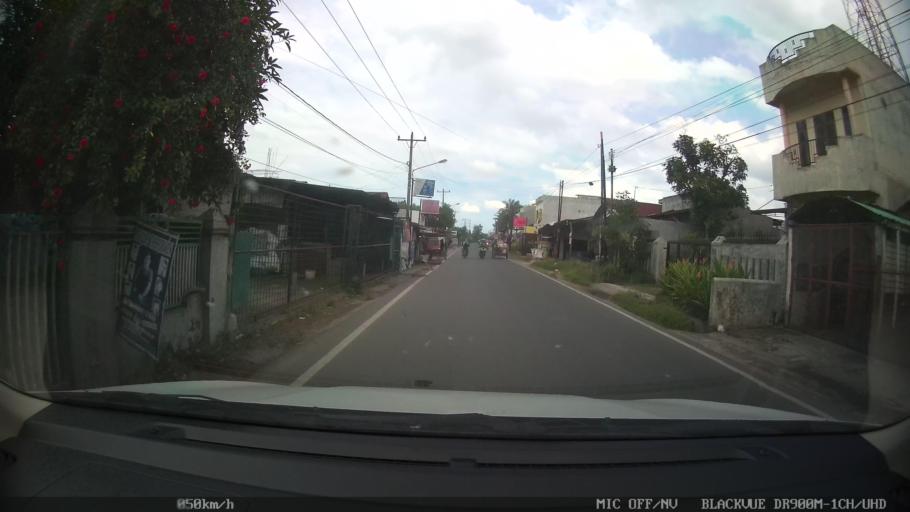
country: ID
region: North Sumatra
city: Sunggal
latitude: 3.6186
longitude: 98.6083
